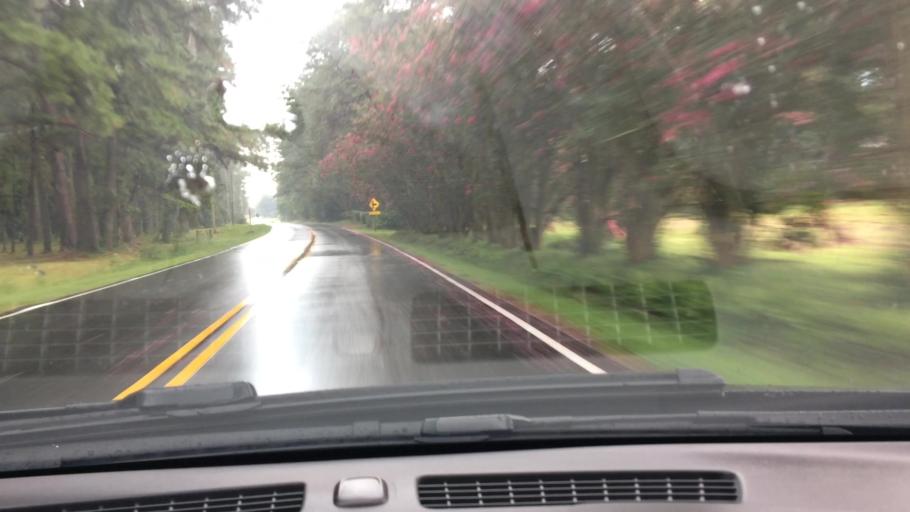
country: US
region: North Carolina
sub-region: Pitt County
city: Winterville
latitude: 35.5056
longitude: -77.3811
